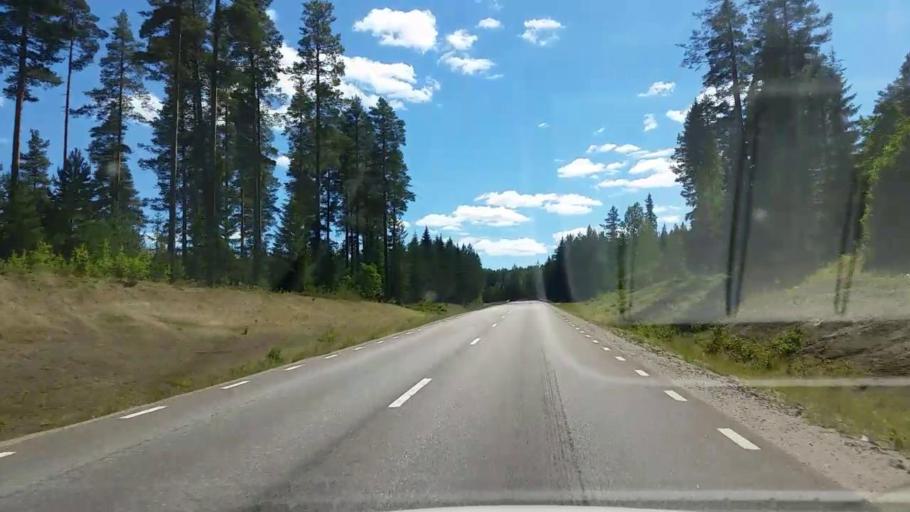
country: SE
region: Gaevleborg
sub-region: Bollnas Kommun
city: Vittsjo
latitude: 61.1624
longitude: 15.8820
